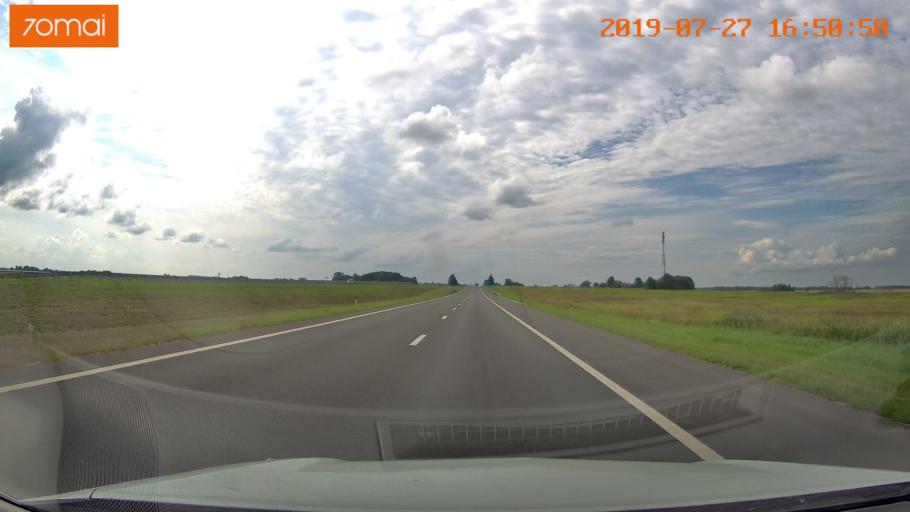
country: RU
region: Kaliningrad
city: Gvardeysk
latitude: 54.6795
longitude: 20.9033
